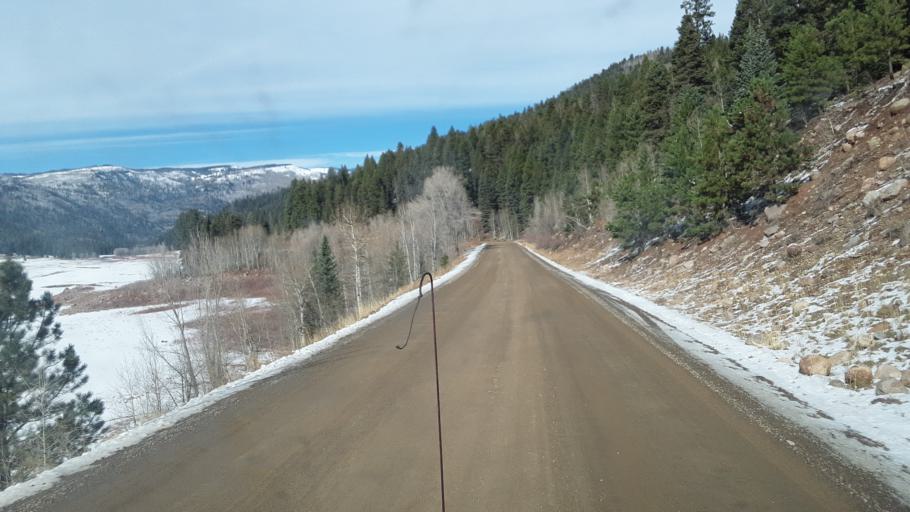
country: US
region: Colorado
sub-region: La Plata County
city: Bayfield
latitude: 37.4089
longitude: -107.6619
